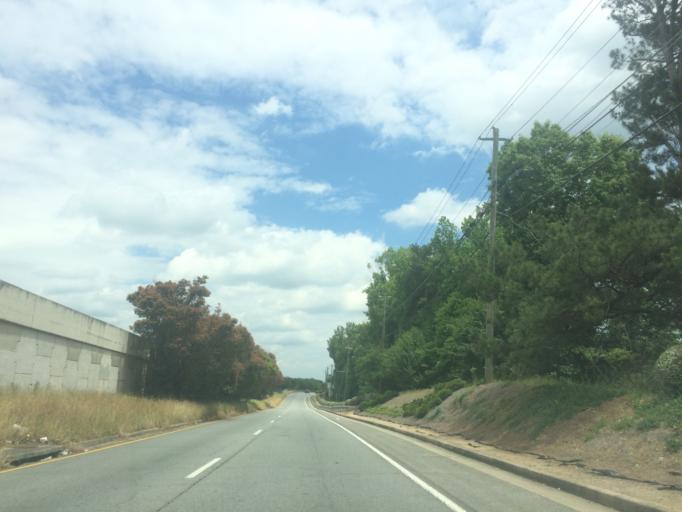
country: US
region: Georgia
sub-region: DeKalb County
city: Chamblee
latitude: 33.8583
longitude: -84.2934
